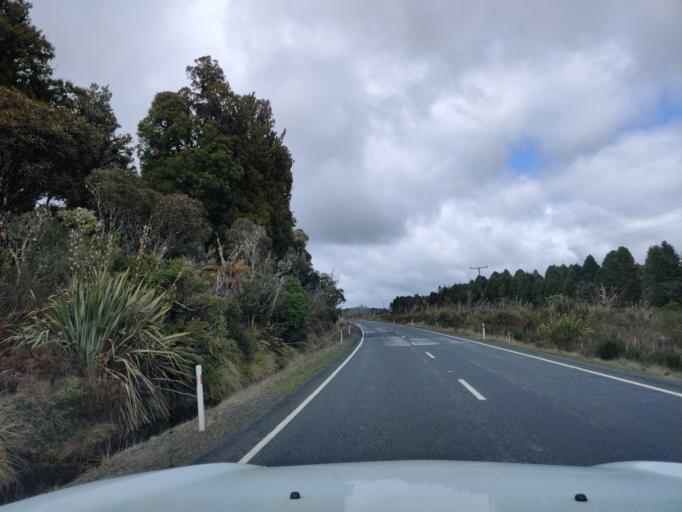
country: NZ
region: Manawatu-Wanganui
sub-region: Ruapehu District
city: Waiouru
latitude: -39.2473
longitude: 175.3889
